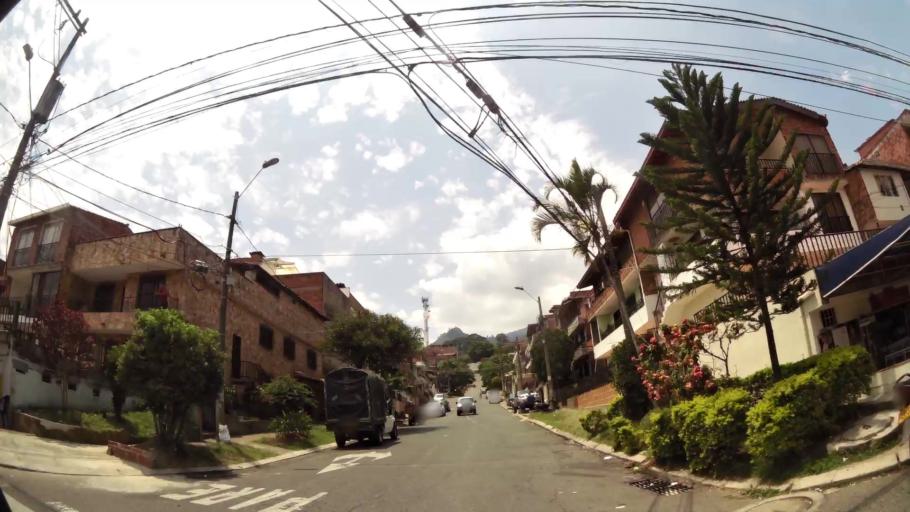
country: CO
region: Antioquia
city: Bello
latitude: 6.3047
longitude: -75.5678
